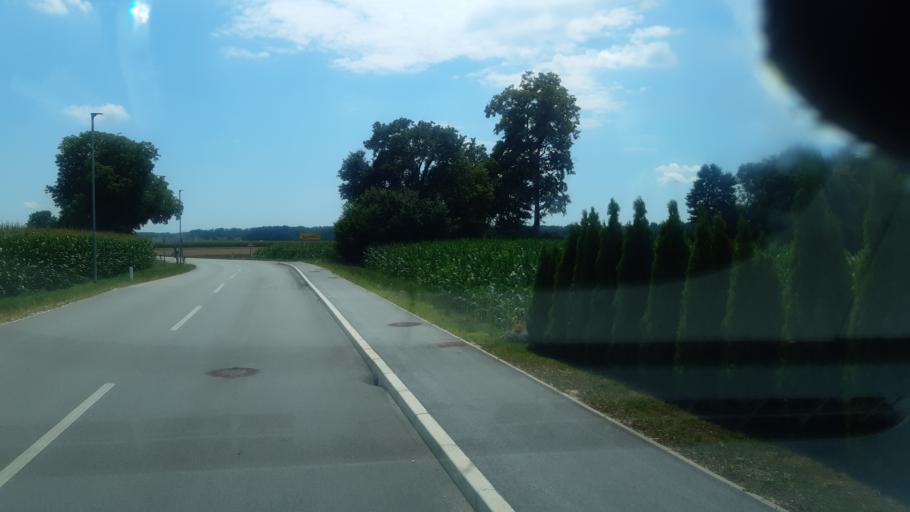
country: SI
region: Moravske Toplice
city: Moravske Toplice
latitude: 46.6814
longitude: 16.1947
